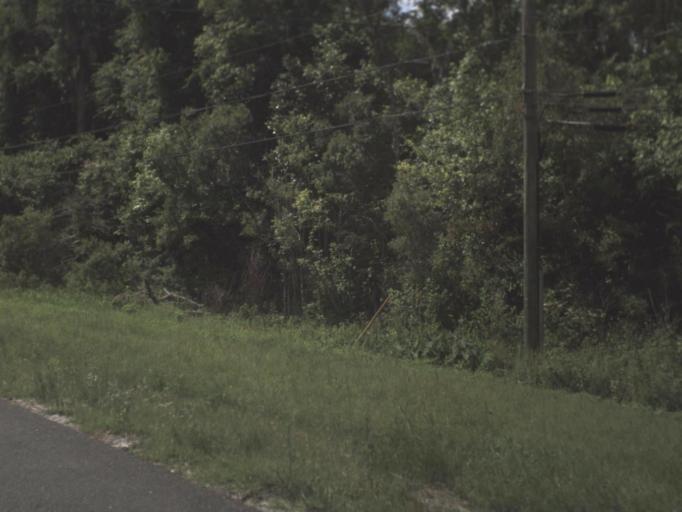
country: US
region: Florida
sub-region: Clay County
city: Green Cove Springs
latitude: 29.9842
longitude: -81.5639
